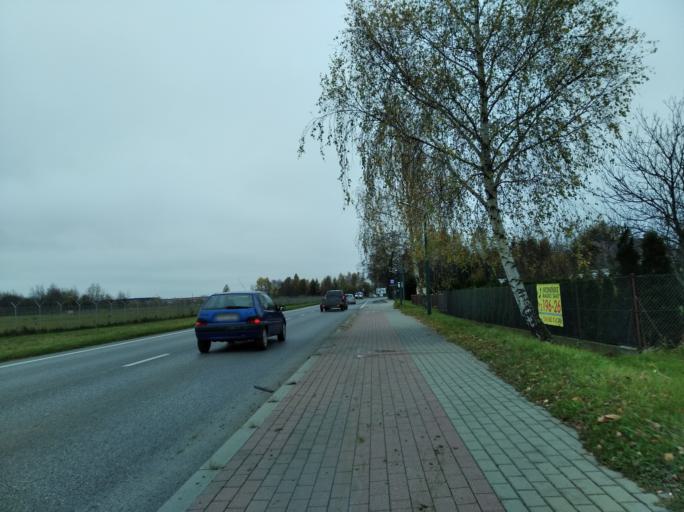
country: PL
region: Subcarpathian Voivodeship
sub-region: Krosno
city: Krosno
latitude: 49.6837
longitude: 21.7233
